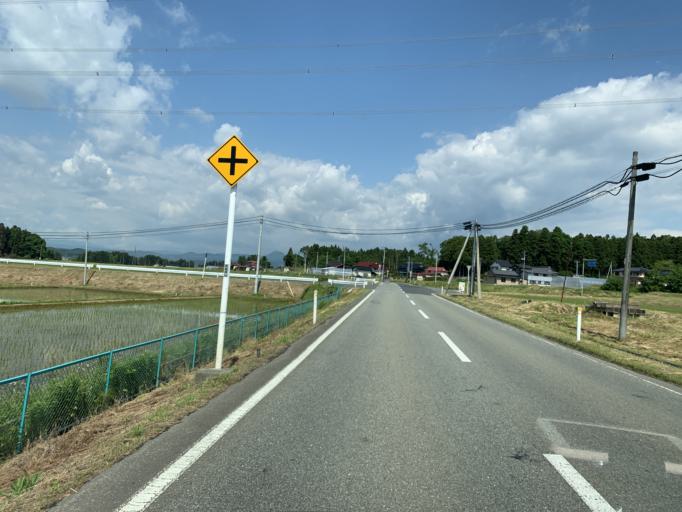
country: JP
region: Iwate
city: Ichinoseki
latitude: 38.8028
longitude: 141.0114
